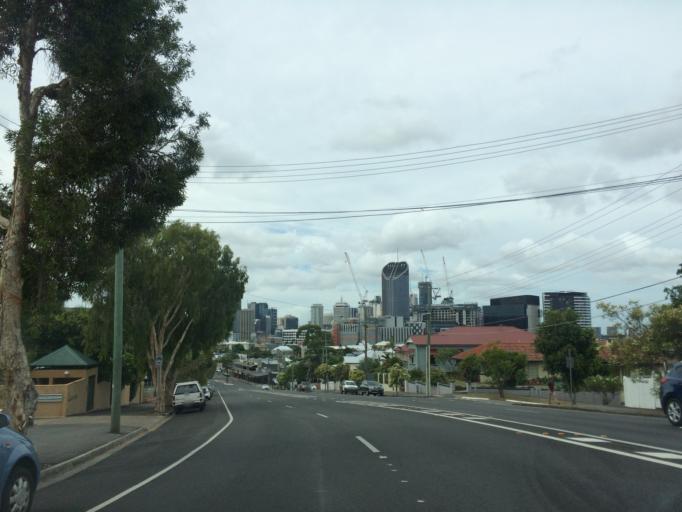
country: AU
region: Queensland
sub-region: Brisbane
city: South Brisbane
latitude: -27.4871
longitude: 153.0192
